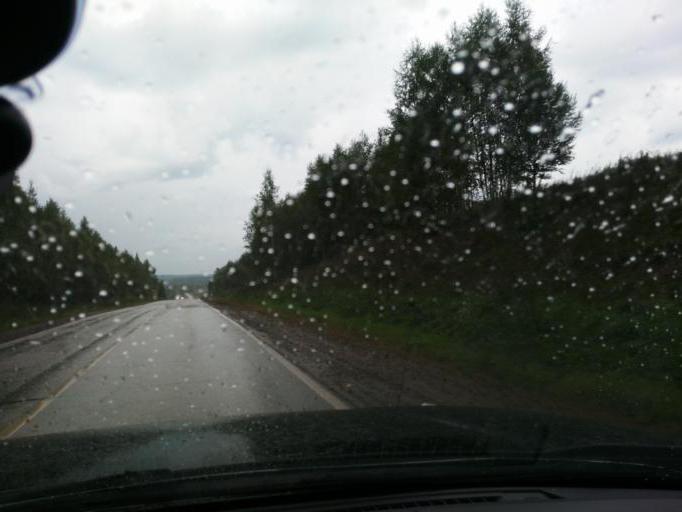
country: RU
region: Perm
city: Barda
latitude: 56.8693
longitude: 55.8898
